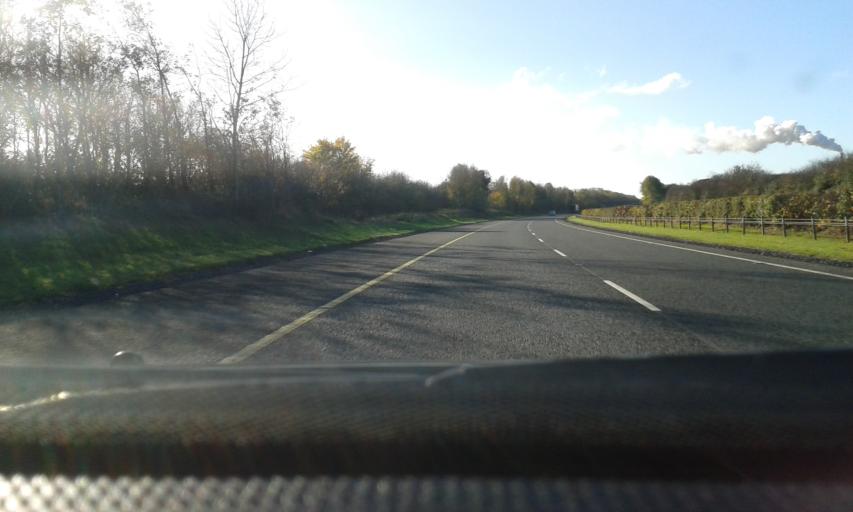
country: IE
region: Leinster
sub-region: Laois
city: Portlaoise
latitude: 53.0356
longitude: -7.2458
